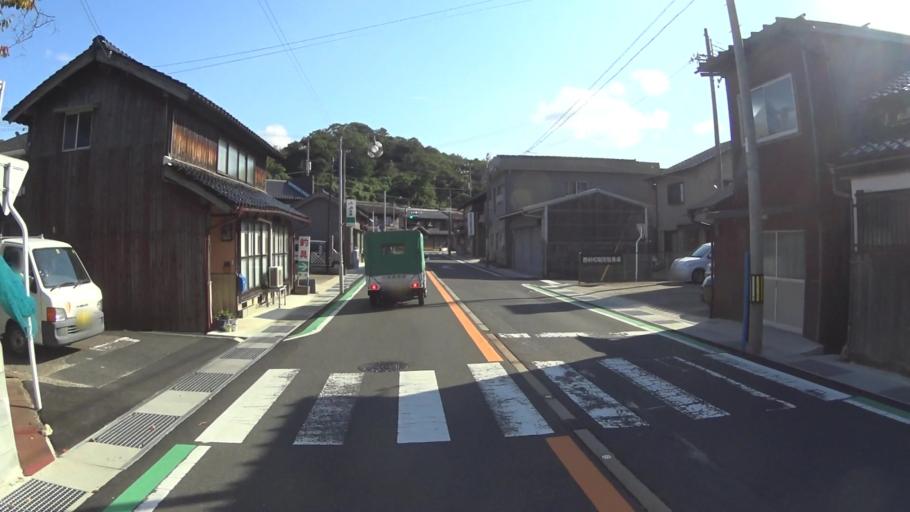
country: JP
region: Kyoto
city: Miyazu
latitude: 35.6805
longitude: 135.0303
